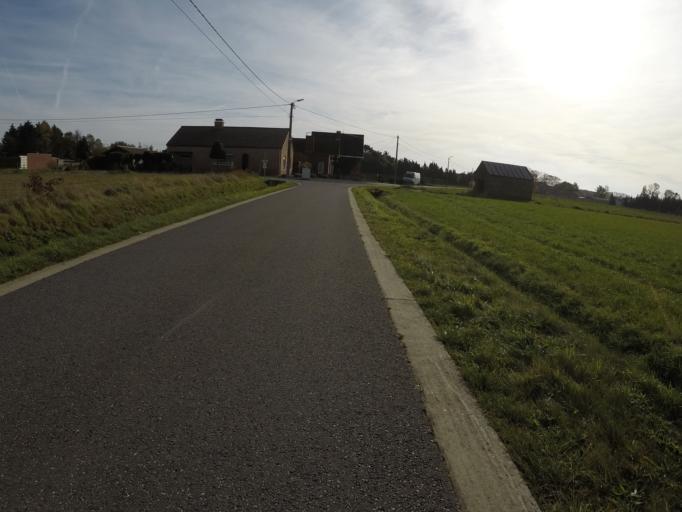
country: BE
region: Flanders
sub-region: Provincie Vlaams-Brabant
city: Begijnendijk
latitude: 51.0346
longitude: 4.7749
